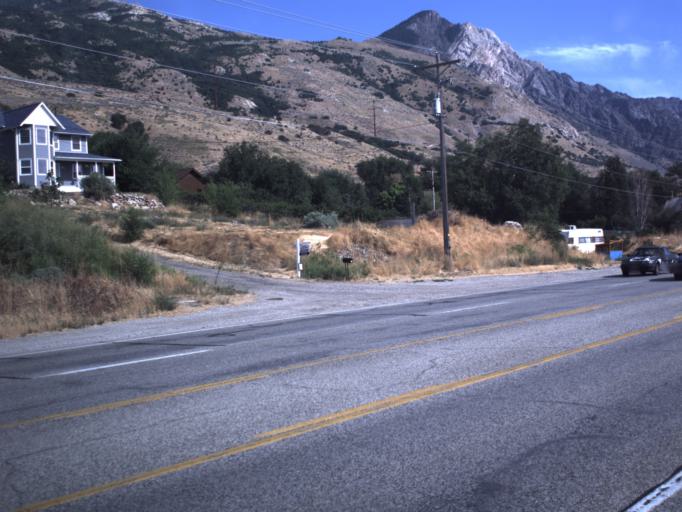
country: US
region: Utah
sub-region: Box Elder County
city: Perry
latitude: 41.4395
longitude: -112.0367
